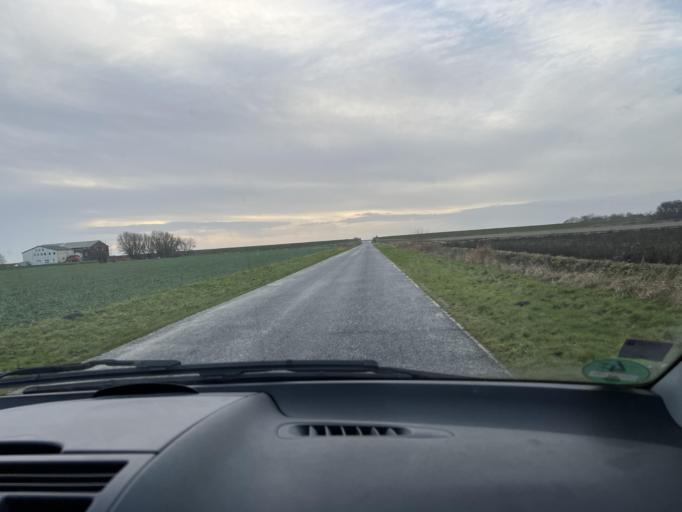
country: DE
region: Schleswig-Holstein
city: Hedwigenkoog
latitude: 54.1776
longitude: 8.8296
